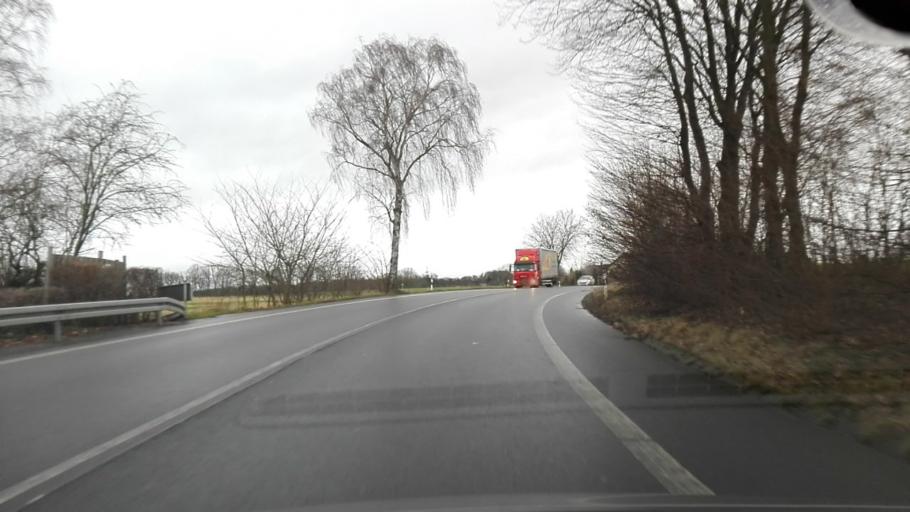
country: DE
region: North Rhine-Westphalia
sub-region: Regierungsbezirk Arnsberg
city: Unna
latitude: 51.4825
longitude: 7.7074
